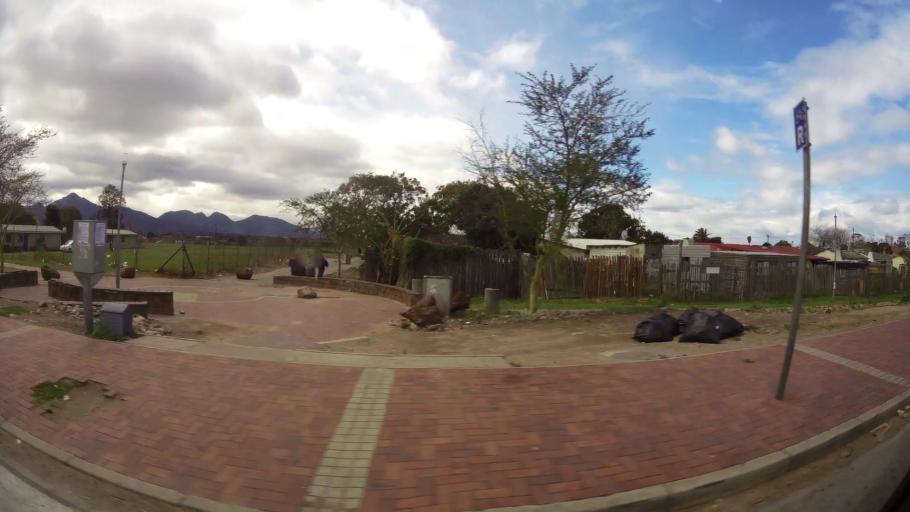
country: ZA
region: Western Cape
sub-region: Eden District Municipality
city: George
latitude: -33.9849
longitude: 22.4730
